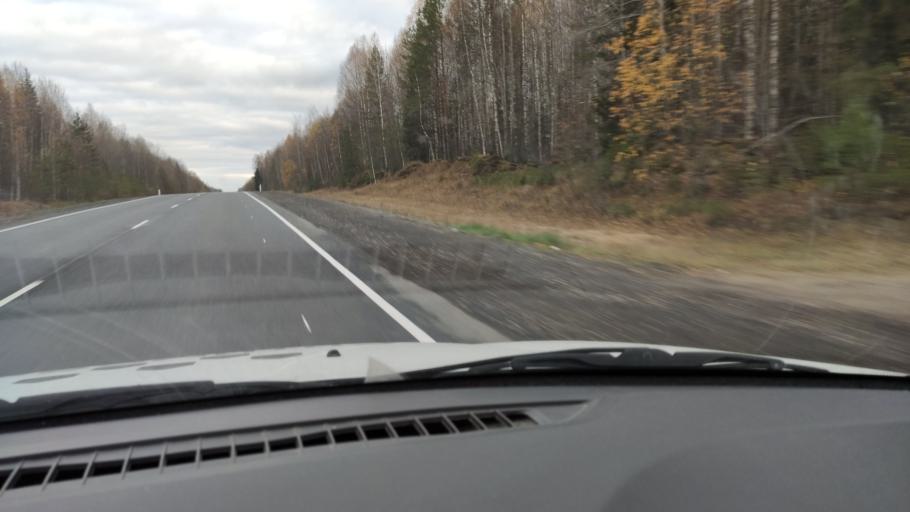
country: RU
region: Kirov
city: Chernaya Kholunitsa
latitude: 58.8822
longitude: 51.4248
